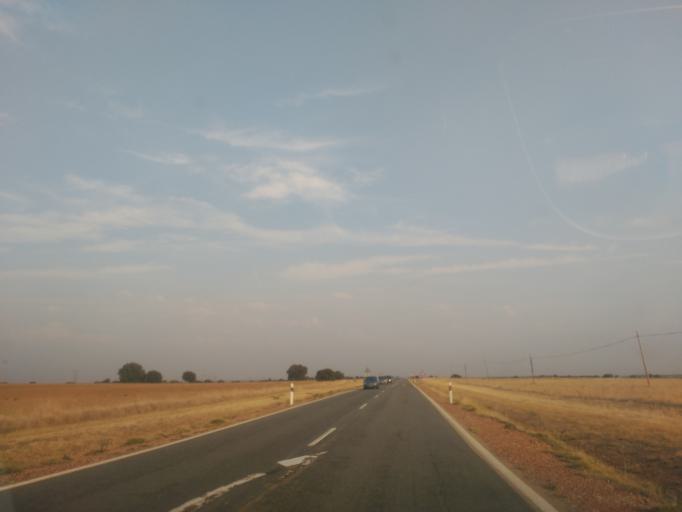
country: ES
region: Castille and Leon
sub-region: Provincia de Zamora
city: Perilla de Castro
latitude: 41.7438
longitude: -5.8372
